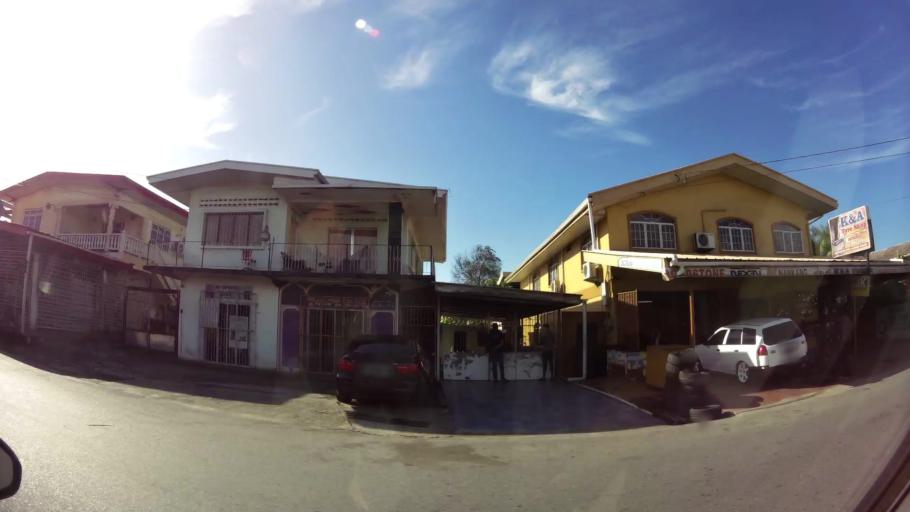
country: TT
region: Chaguanas
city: Chaguanas
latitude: 10.5135
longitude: -61.3813
